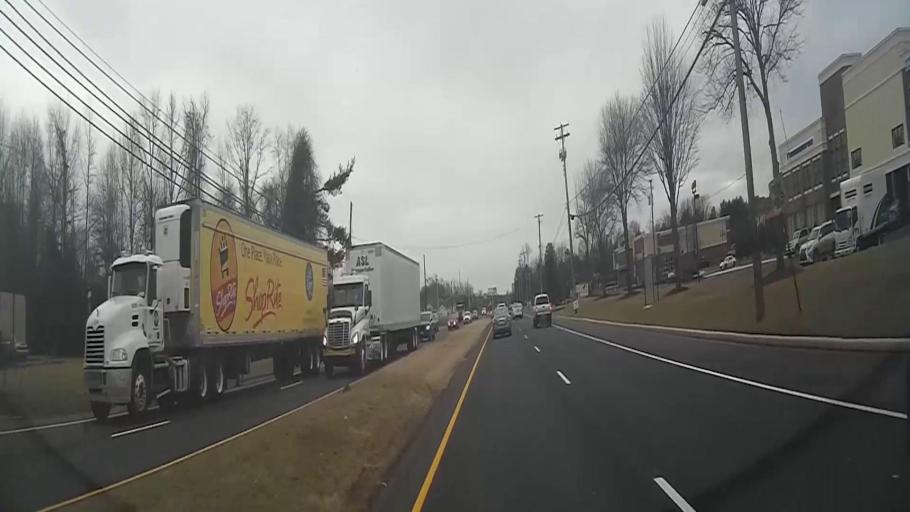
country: US
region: New Jersey
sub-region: Burlington County
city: Marlton
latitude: 39.8618
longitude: -74.9218
